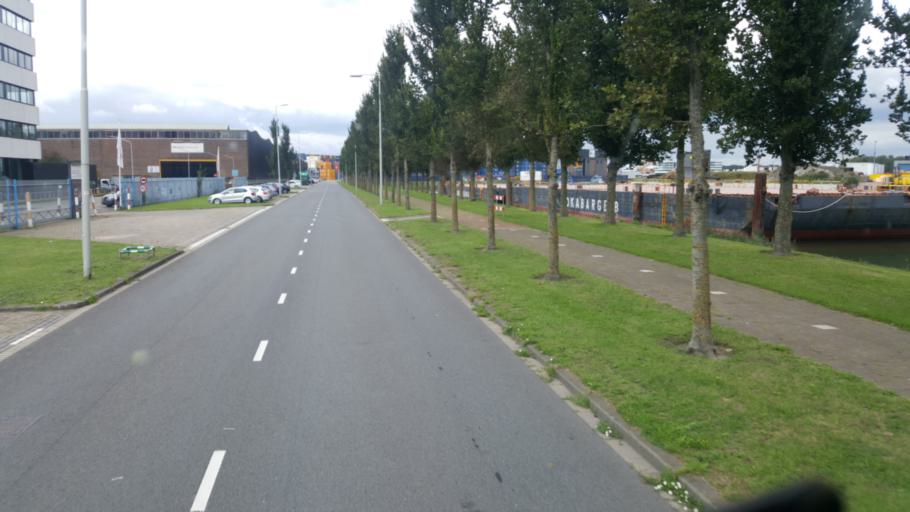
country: NL
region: South Holland
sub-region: Gemeente Schiedam
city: Schiedam
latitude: 51.8923
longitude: 4.4095
